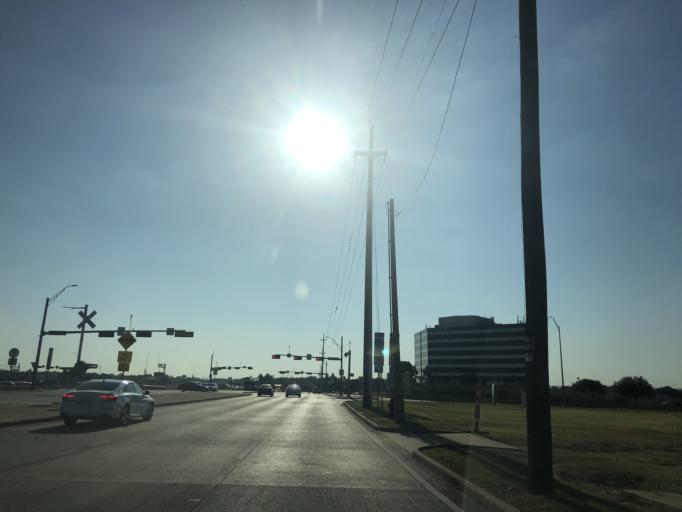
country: US
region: Texas
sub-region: Dallas County
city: Grand Prairie
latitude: 32.7407
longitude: -97.0215
